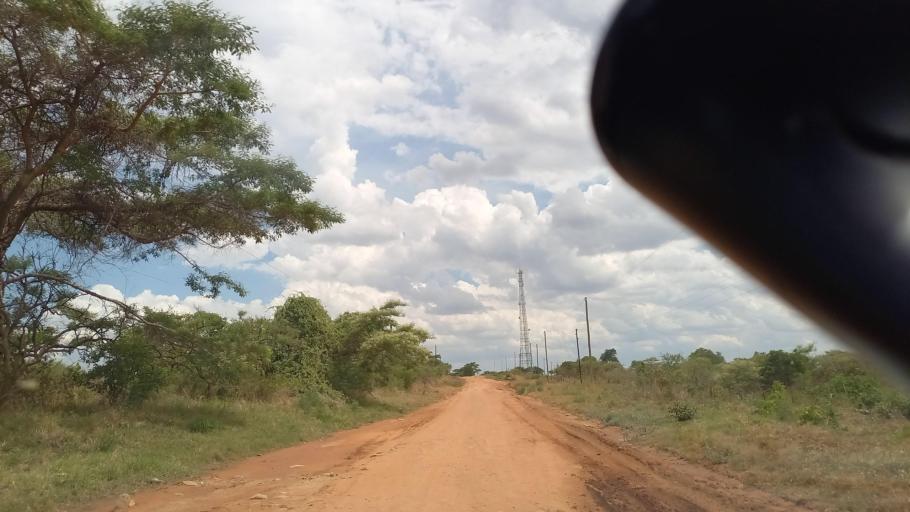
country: ZM
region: Southern
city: Nakambala
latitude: -16.0331
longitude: 27.9695
